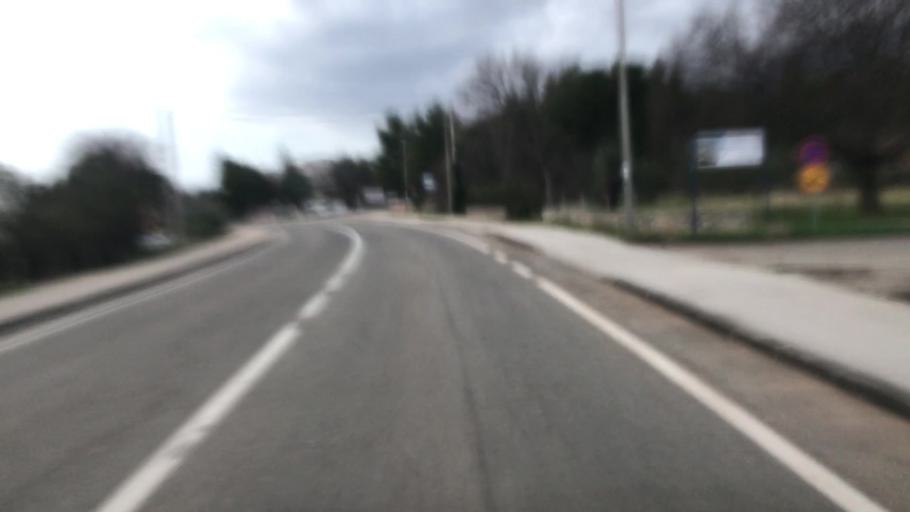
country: HR
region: Zadarska
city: Starigrad
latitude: 44.2881
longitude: 15.4484
